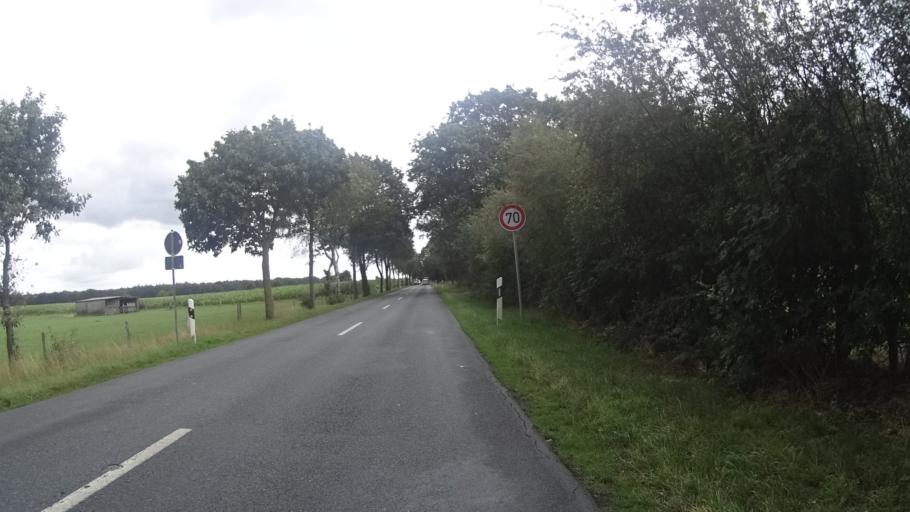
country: DE
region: Lower Saxony
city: Kuhrstedt
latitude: 53.5788
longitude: 8.7718
